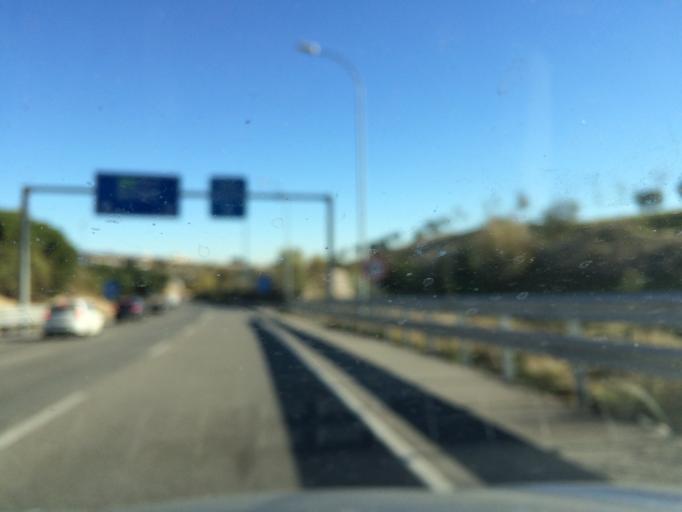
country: ES
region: Madrid
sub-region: Provincia de Madrid
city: Las Tablas
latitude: 40.5100
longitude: -3.6628
